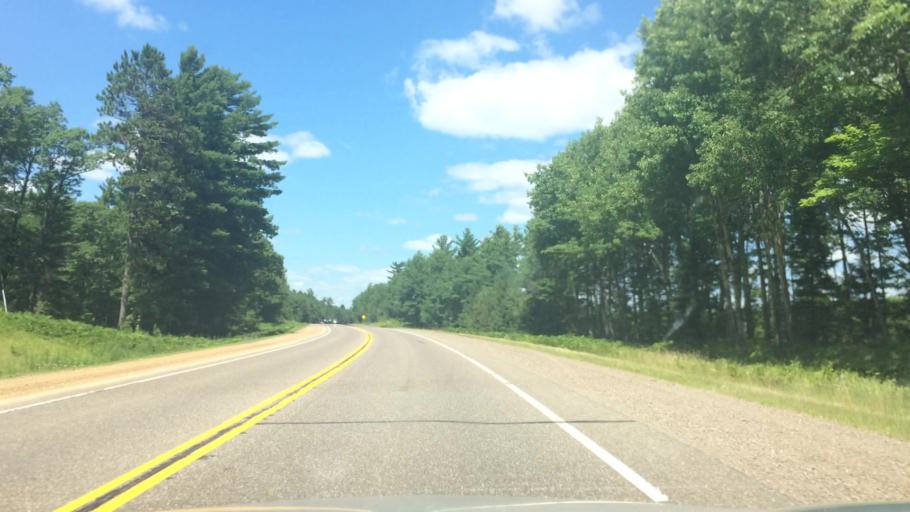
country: US
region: Wisconsin
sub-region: Vilas County
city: Lac du Flambeau
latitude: 45.9427
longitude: -89.6970
